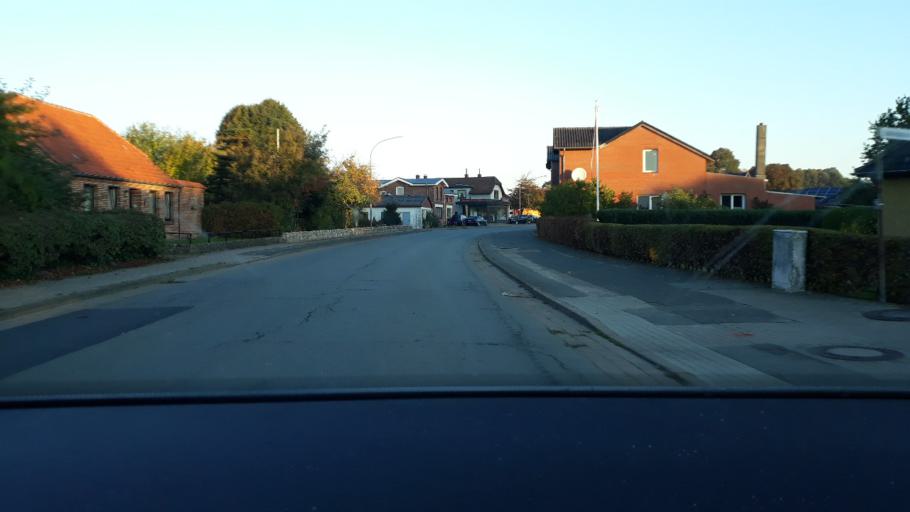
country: DE
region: Schleswig-Holstein
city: Satrup
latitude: 54.6866
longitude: 9.6026
